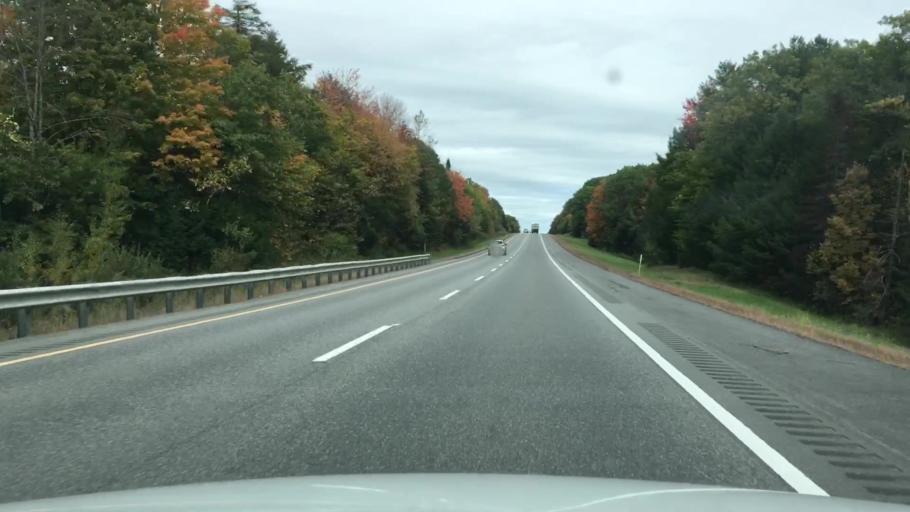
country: US
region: Maine
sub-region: Kennebec County
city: Sidney
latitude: 44.4007
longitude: -69.7524
